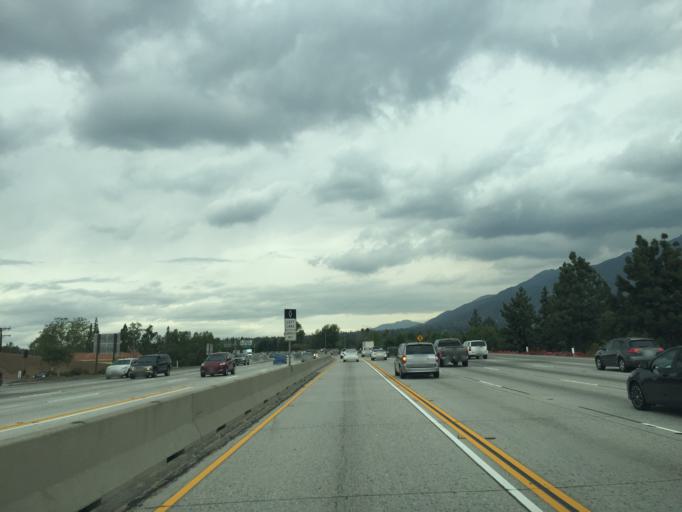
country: US
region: California
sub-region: Los Angeles County
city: Arcadia
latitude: 34.1469
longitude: -118.0291
